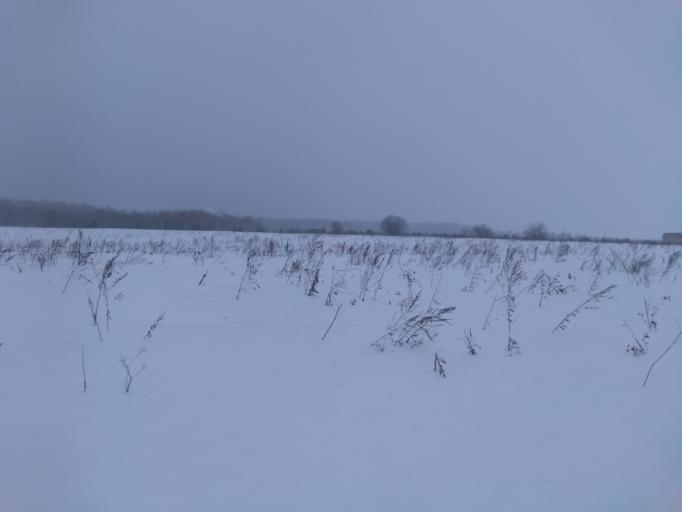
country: RU
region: Perm
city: Sylva
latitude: 57.8447
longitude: 56.7865
